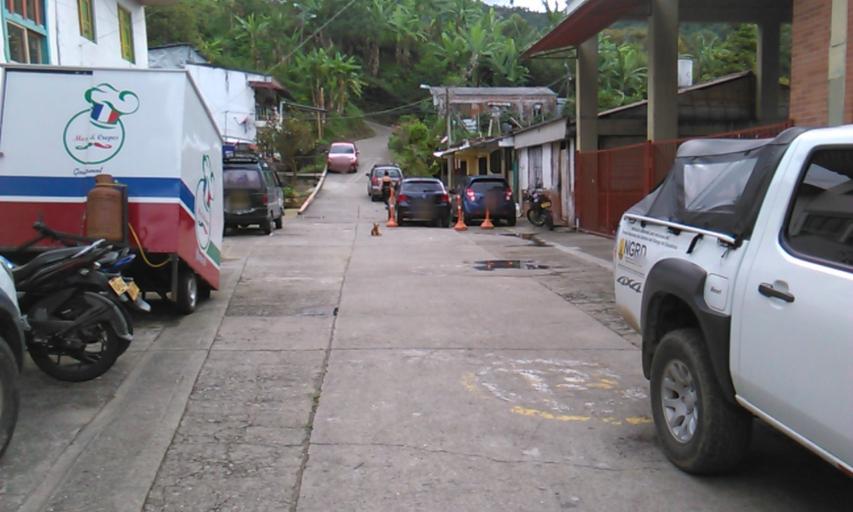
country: CO
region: Quindio
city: Cordoba
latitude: 4.3901
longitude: -75.6859
